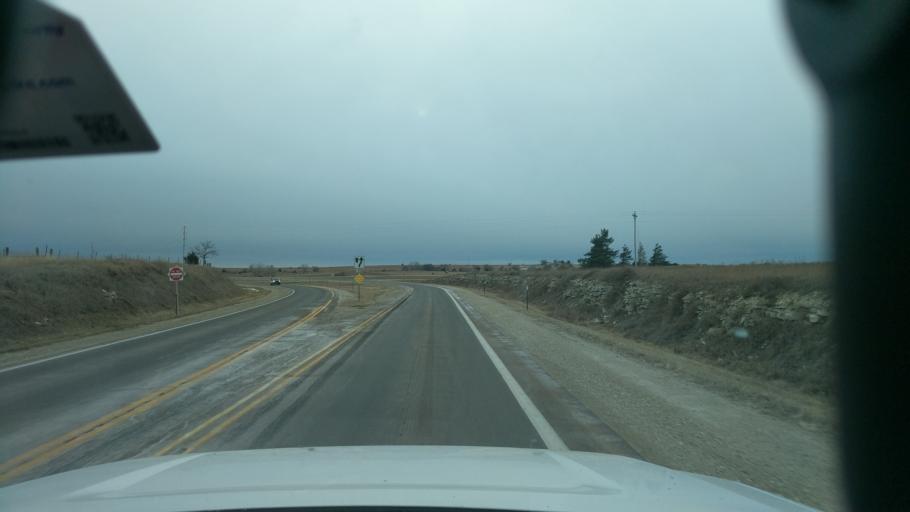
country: US
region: Kansas
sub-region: Dickinson County
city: Herington
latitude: 38.6447
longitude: -96.9468
